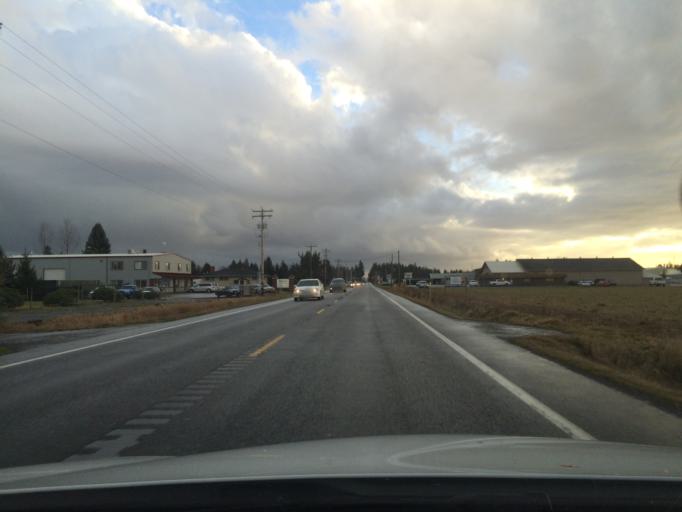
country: US
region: Washington
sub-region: Whatcom County
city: Lynden
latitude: 48.9513
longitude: -122.4852
